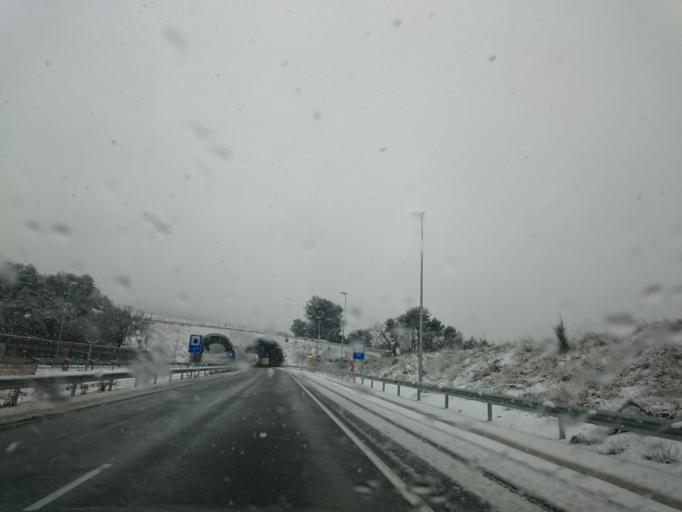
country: ES
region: Catalonia
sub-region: Provincia de Barcelona
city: Sant Pere de Ribes
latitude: 41.2812
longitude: 1.7290
